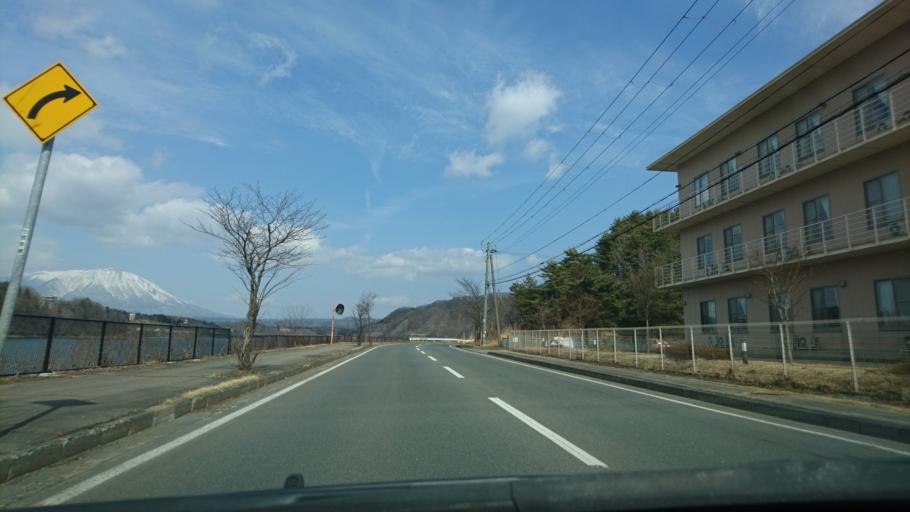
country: JP
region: Iwate
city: Shizukuishi
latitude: 39.6811
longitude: 141.0264
